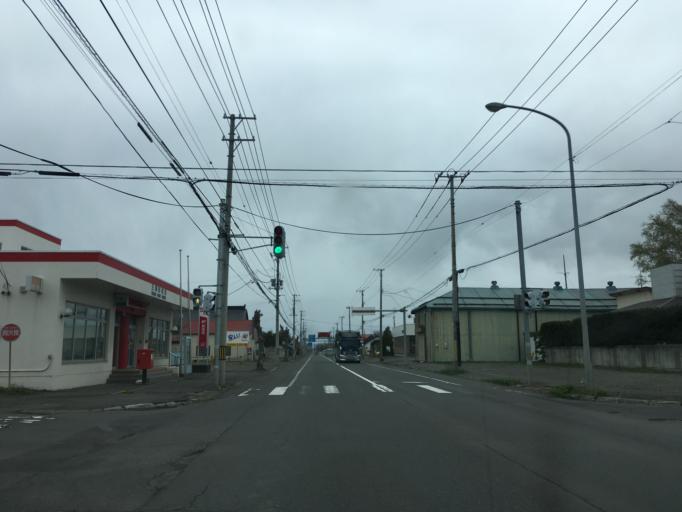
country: JP
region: Hokkaido
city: Chitose
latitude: 42.9453
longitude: 141.8036
